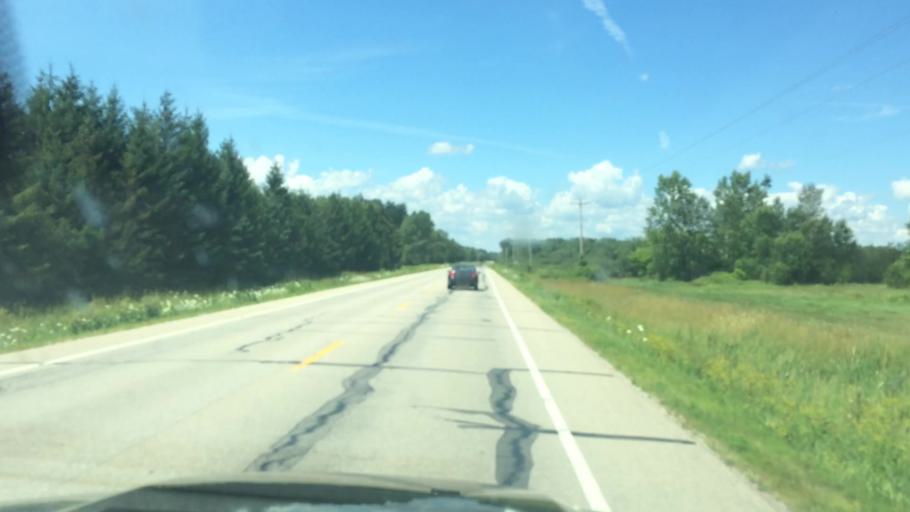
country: US
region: Wisconsin
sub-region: Marinette County
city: Peshtigo
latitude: 45.1001
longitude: -87.7156
